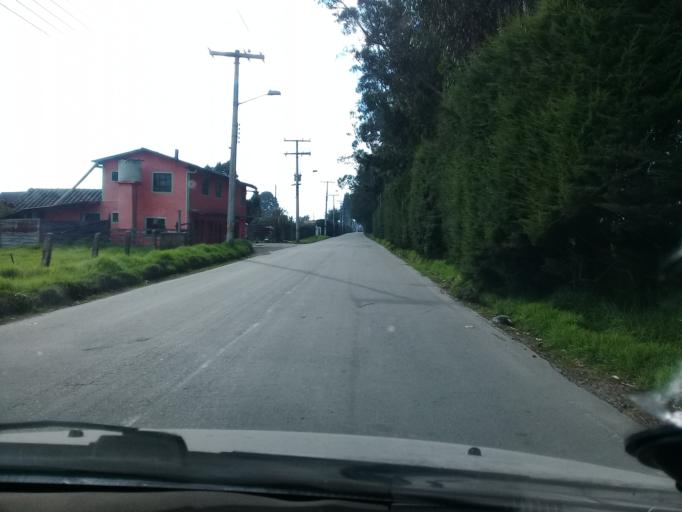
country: CO
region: Cundinamarca
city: El Rosal
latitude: 4.8181
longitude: -74.2385
